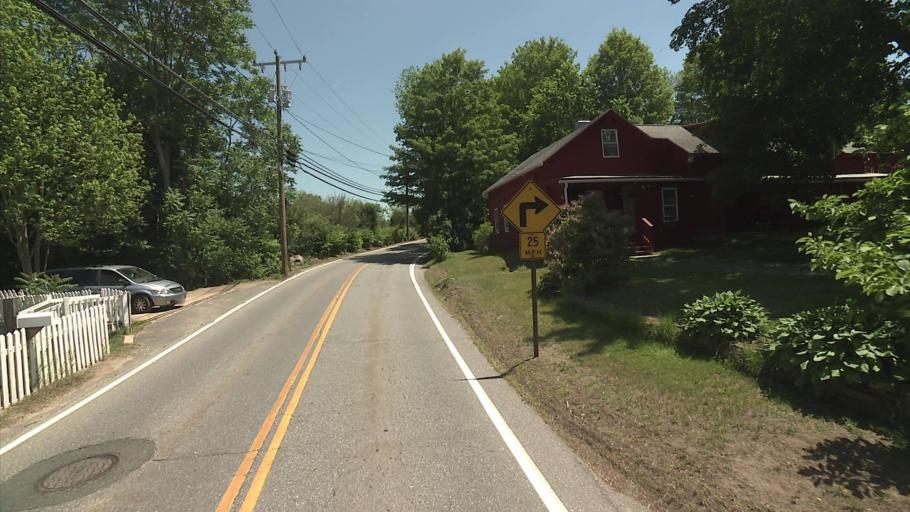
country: US
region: Connecticut
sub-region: Tolland County
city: Stafford
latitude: 41.9848
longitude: -72.2917
